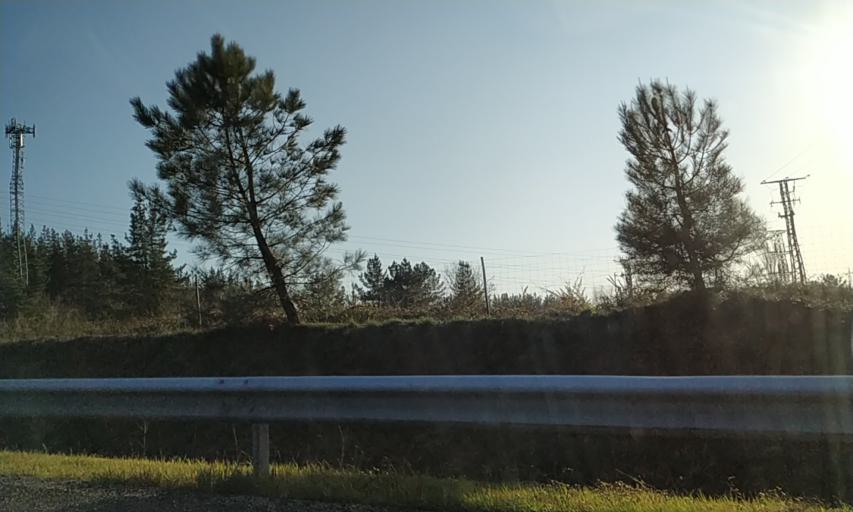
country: ES
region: Galicia
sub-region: Provincia de Lugo
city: O Paramo
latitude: 42.9260
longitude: -7.3584
